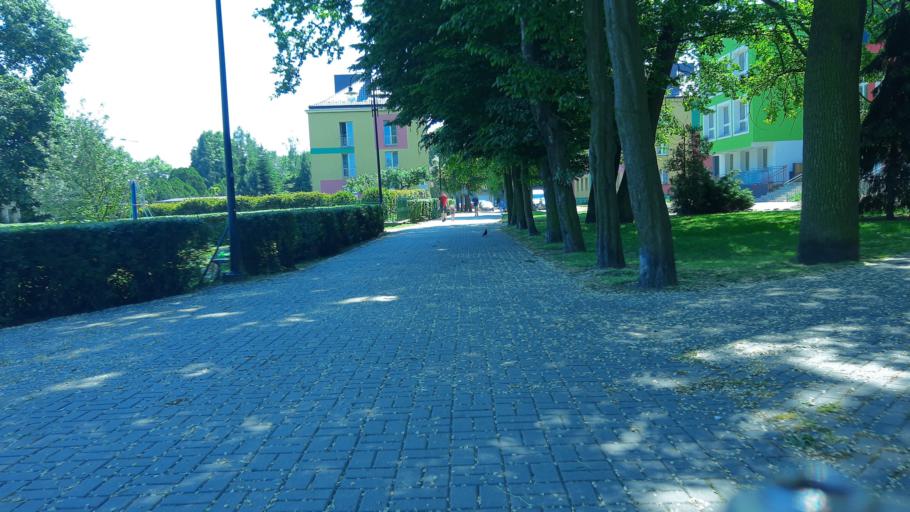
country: PL
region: Lodz Voivodeship
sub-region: Powiat sieradzki
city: Sieradz
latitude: 51.5926
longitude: 18.7342
